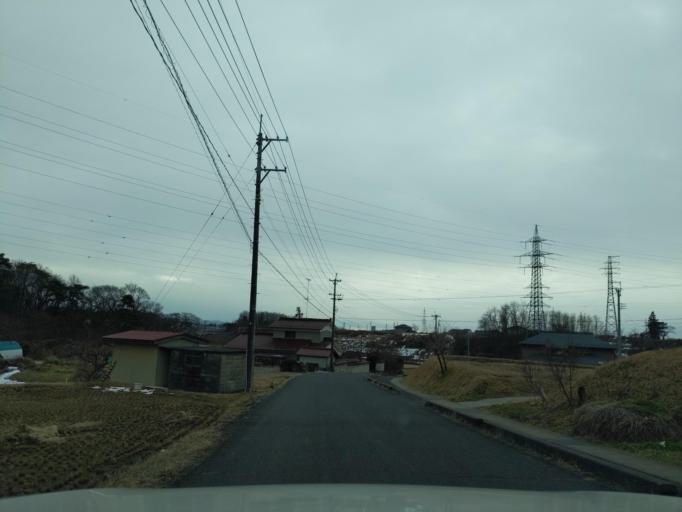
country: JP
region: Fukushima
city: Koriyama
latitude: 37.4526
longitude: 140.3854
